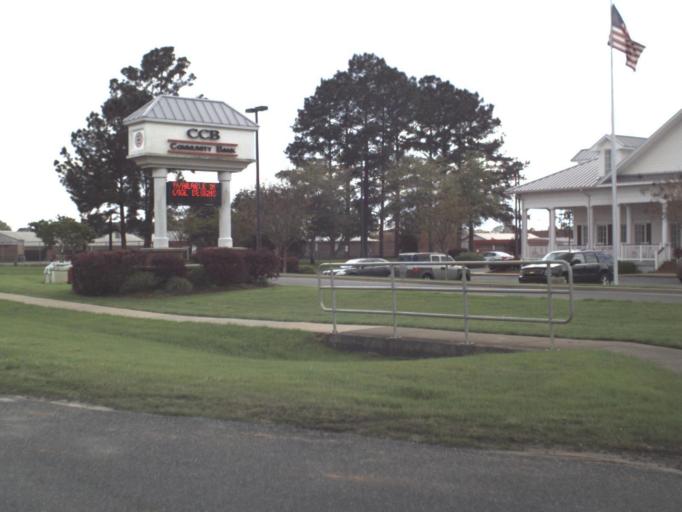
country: US
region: Florida
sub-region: Okaloosa County
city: Crestview
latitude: 30.7918
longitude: -86.5582
